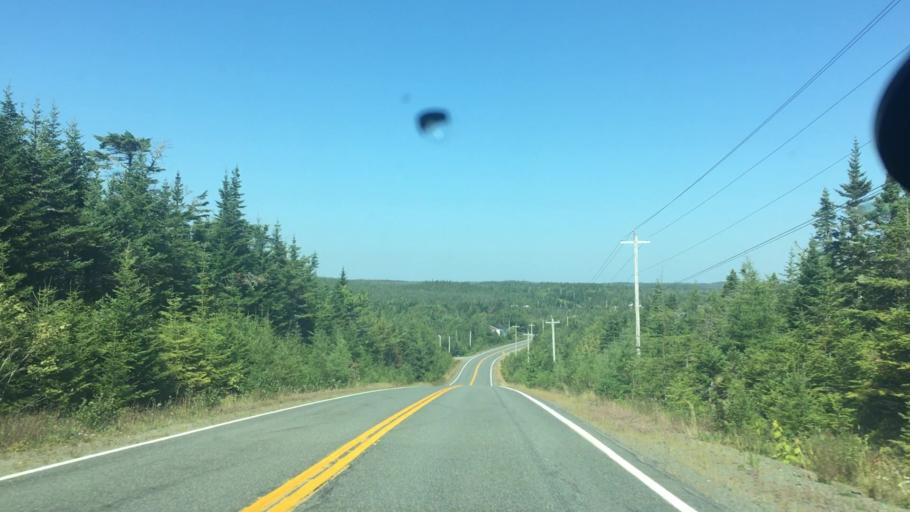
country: CA
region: Nova Scotia
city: Antigonish
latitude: 44.9950
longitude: -62.0985
